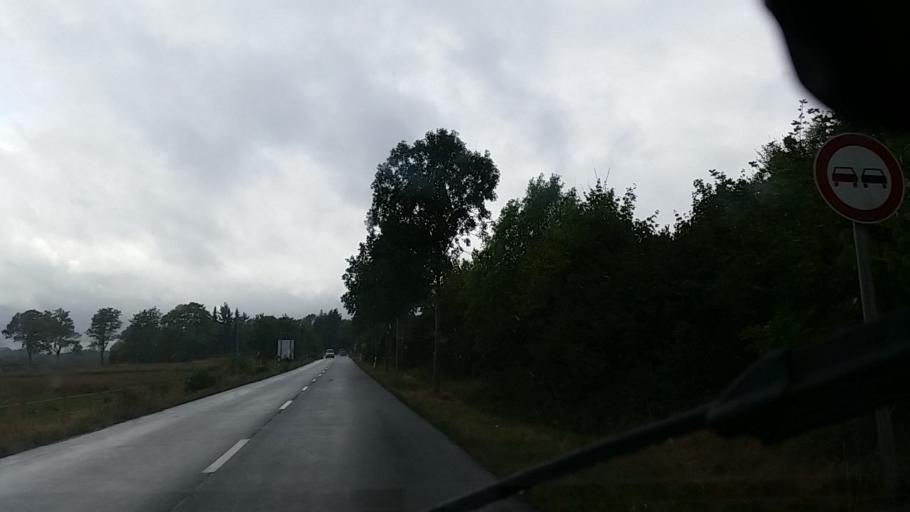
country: DE
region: Lower Saxony
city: Wolfsburg
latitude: 52.3596
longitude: 10.7417
